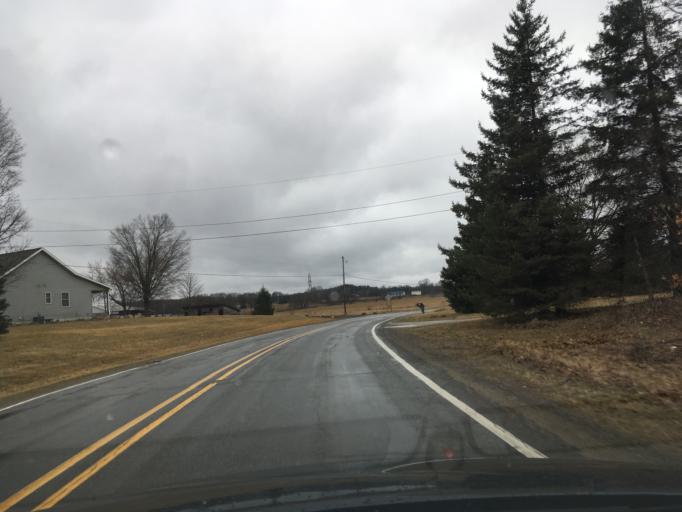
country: US
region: Michigan
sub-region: Washtenaw County
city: Chelsea
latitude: 42.2942
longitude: -84.0687
